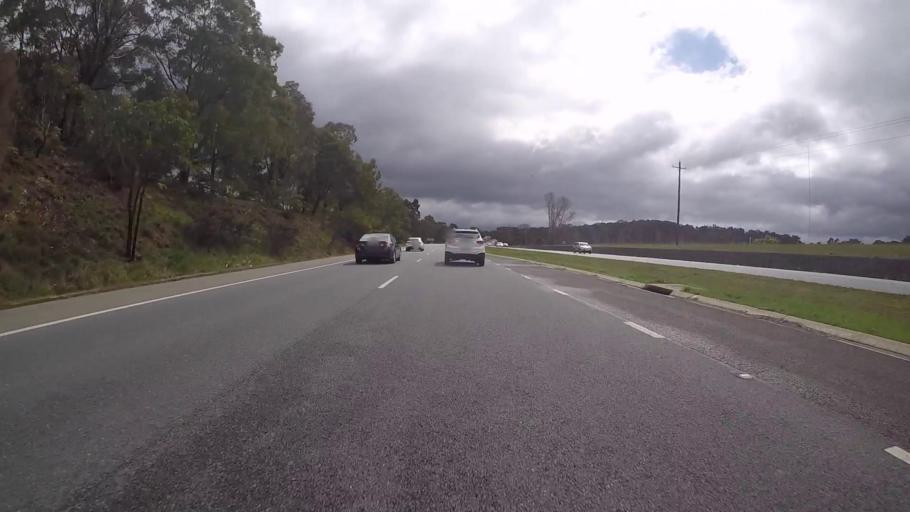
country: AU
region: Australian Capital Territory
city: Kaleen
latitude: -35.2168
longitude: 149.1161
